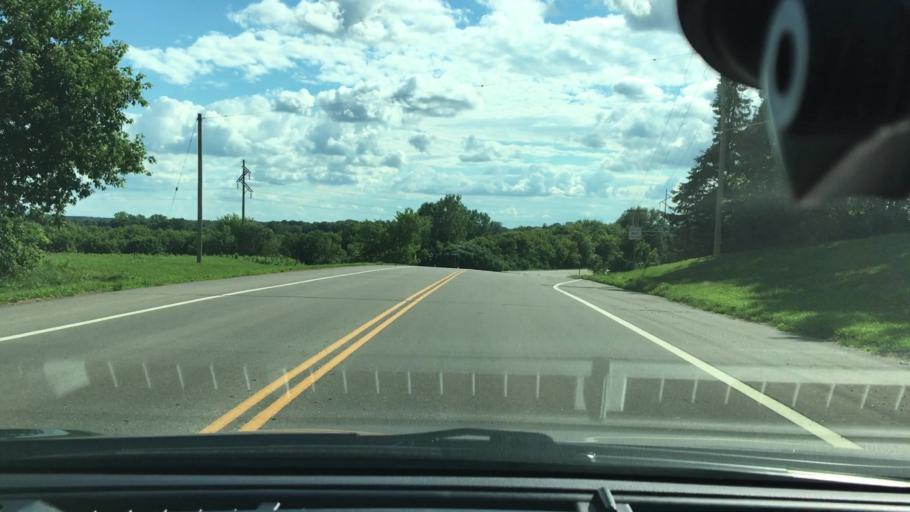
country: US
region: Minnesota
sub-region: Hennepin County
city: Minnetrista
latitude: 44.9214
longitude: -93.7270
